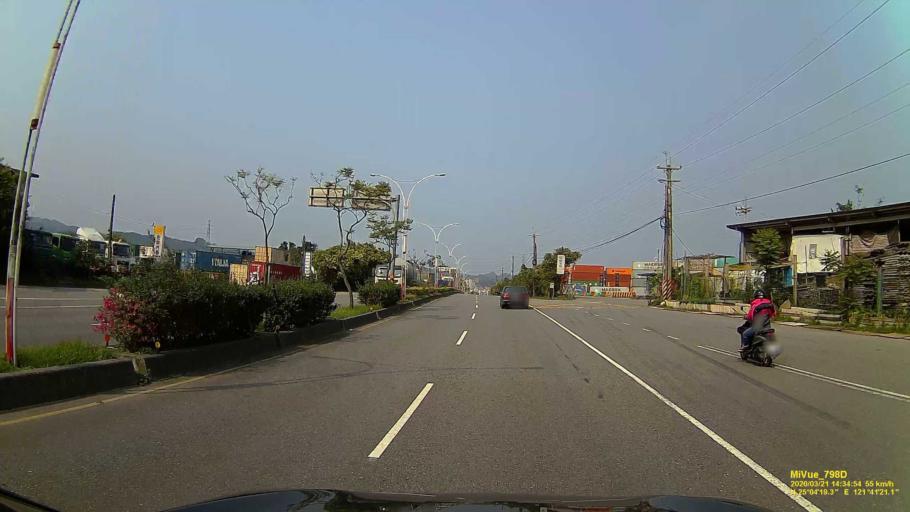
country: TW
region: Taiwan
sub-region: Keelung
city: Keelung
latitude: 25.0721
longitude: 121.6893
